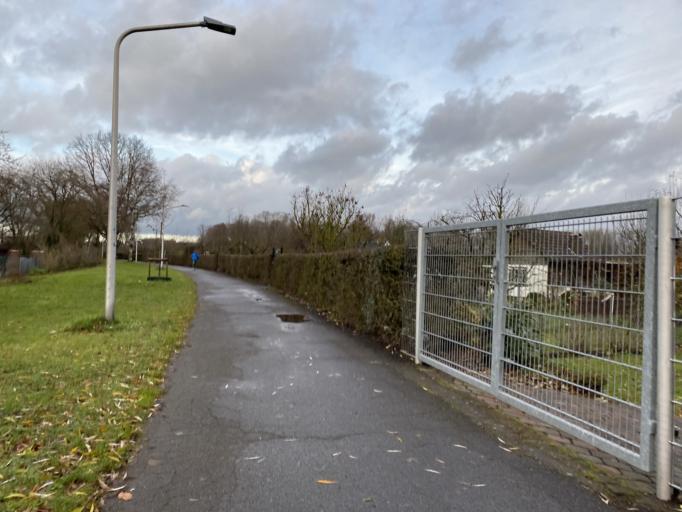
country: DE
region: North Rhine-Westphalia
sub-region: Regierungsbezirk Arnsberg
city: Hamm
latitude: 51.6778
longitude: 7.8465
